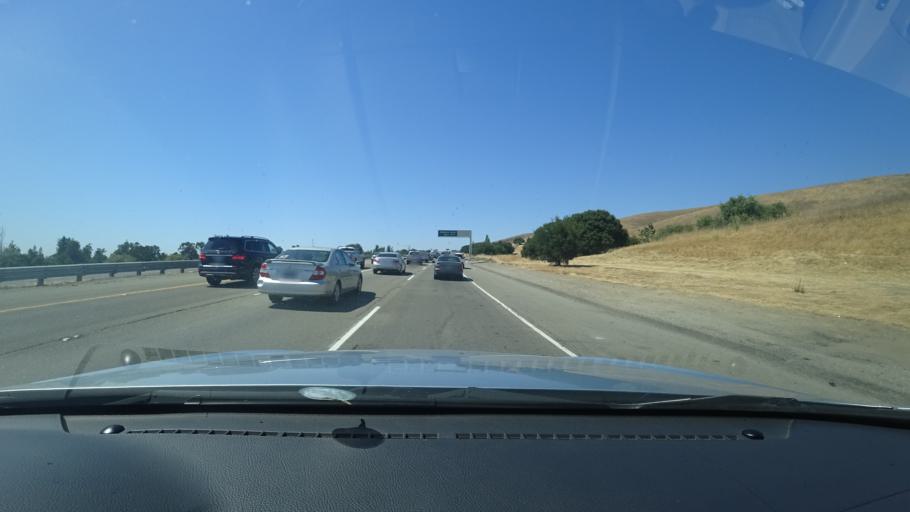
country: US
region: California
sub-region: Santa Clara County
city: Milpitas
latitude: 37.4733
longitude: -121.9102
